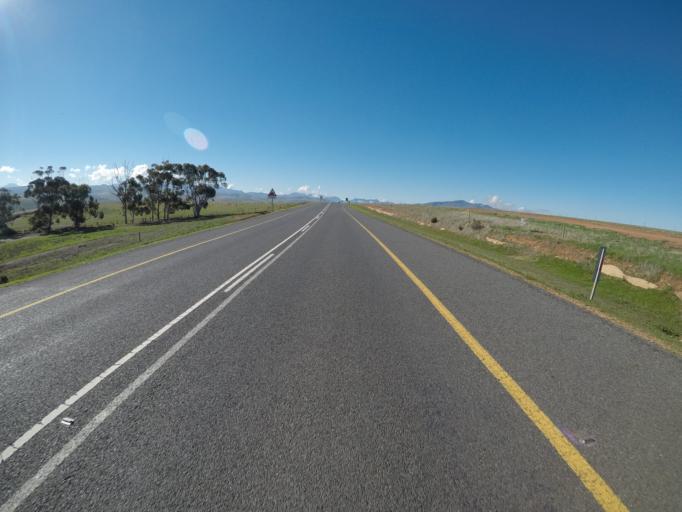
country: ZA
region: Western Cape
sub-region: Overberg District Municipality
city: Caledon
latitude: -34.2200
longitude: 19.3123
